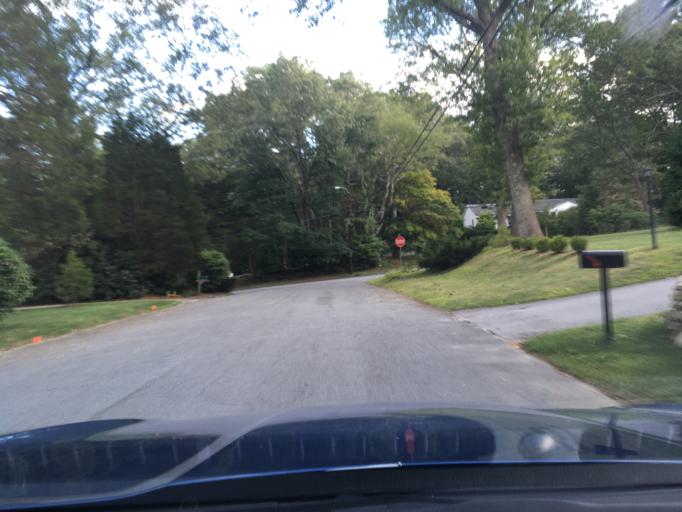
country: US
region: Rhode Island
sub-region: Kent County
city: East Greenwich
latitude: 41.6497
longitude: -71.4822
